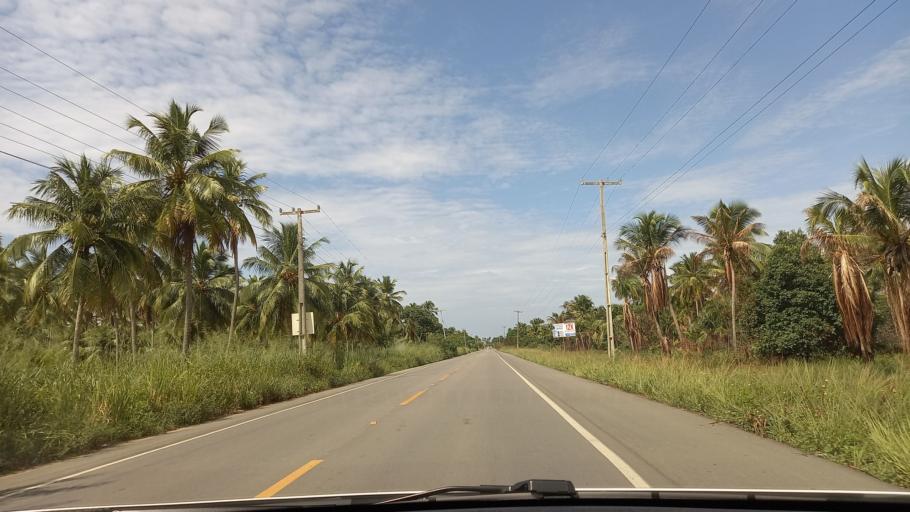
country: BR
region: Alagoas
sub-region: Maragogi
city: Maragogi
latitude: -8.9640
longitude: -35.1810
